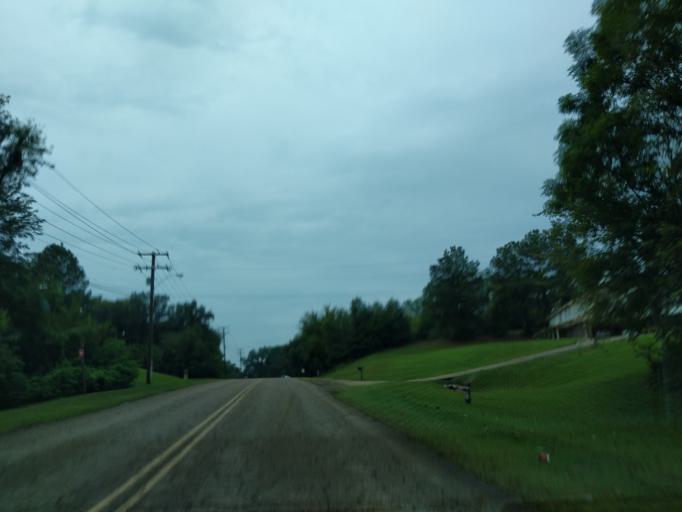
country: US
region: Mississippi
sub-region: Warren County
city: Vicksburg
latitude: 32.3172
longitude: -90.8873
